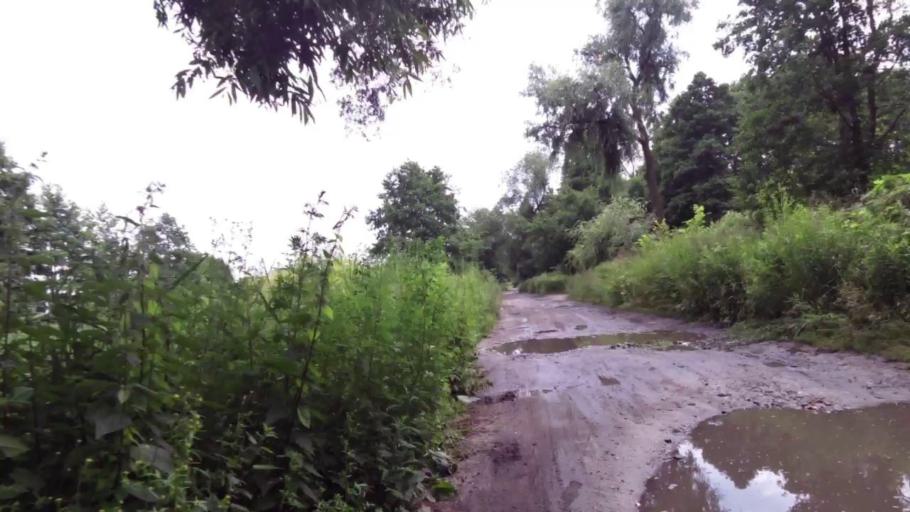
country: PL
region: West Pomeranian Voivodeship
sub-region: Szczecin
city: Szczecin
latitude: 53.4062
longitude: 14.6705
